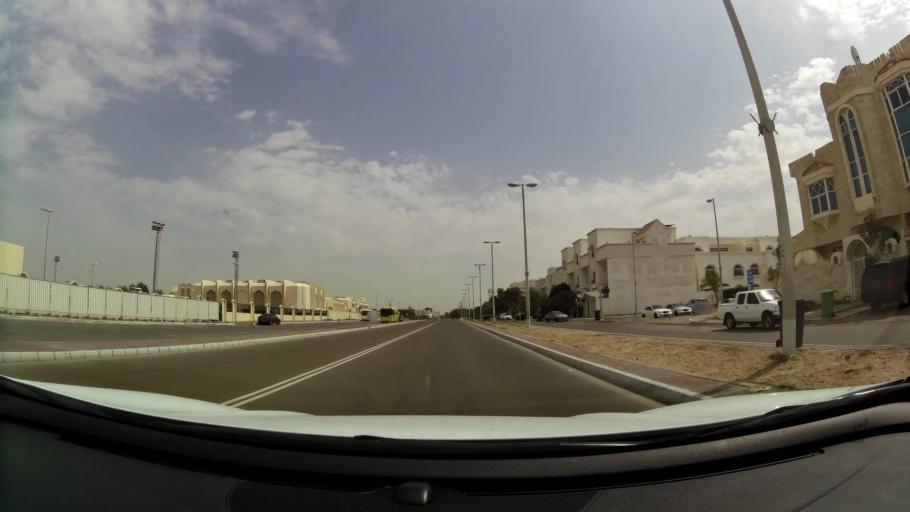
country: AE
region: Abu Dhabi
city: Abu Dhabi
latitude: 24.4611
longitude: 54.3426
